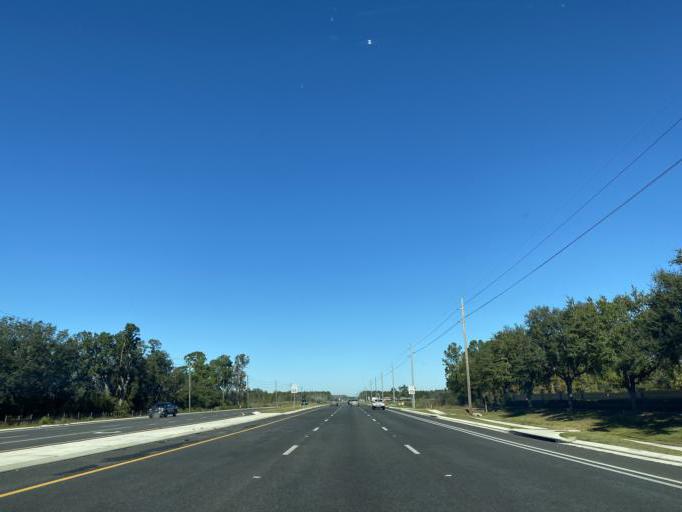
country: US
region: Florida
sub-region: Lake County
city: Four Corners
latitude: 28.4140
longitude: -81.7025
